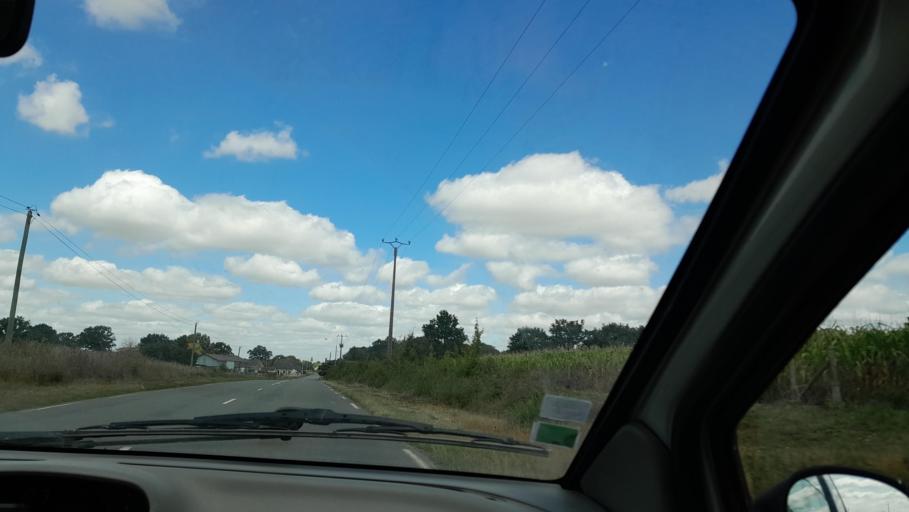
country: FR
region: Pays de la Loire
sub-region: Departement de la Mayenne
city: Ballots
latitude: 47.9314
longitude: -1.0764
